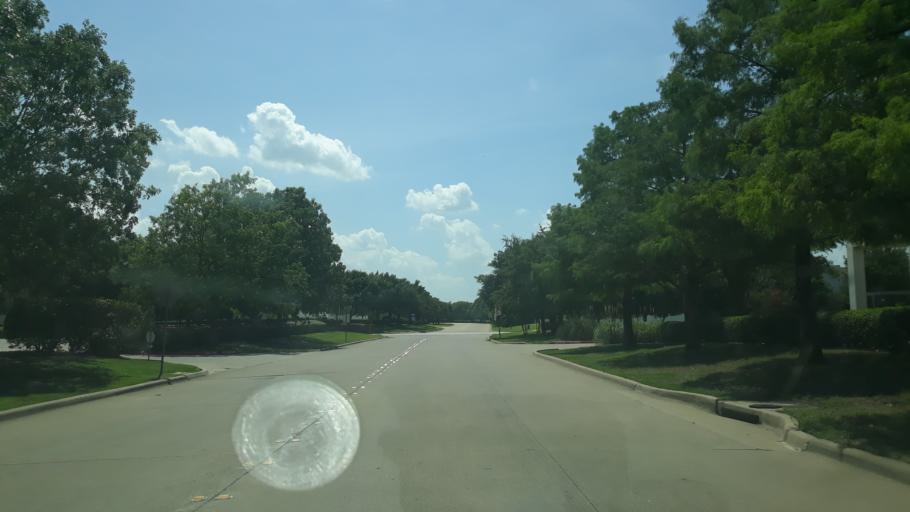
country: US
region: Texas
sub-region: Dallas County
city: Coppell
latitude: 32.9610
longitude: -97.0254
